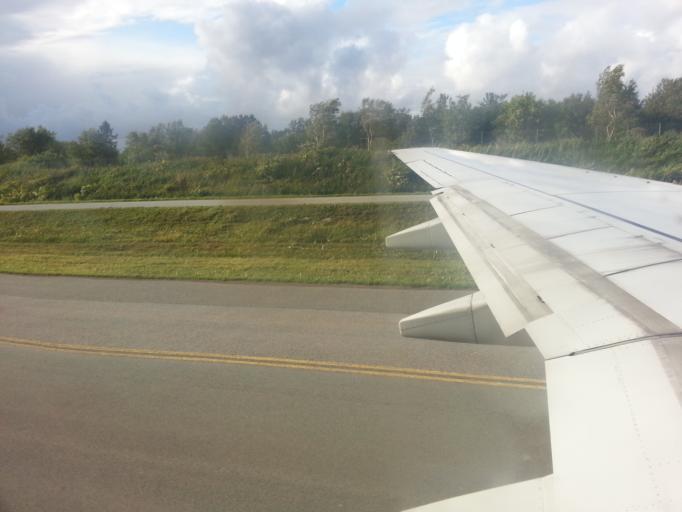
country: NO
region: Nordland
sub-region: Bodo
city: Bodo
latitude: 67.2716
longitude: 14.3801
